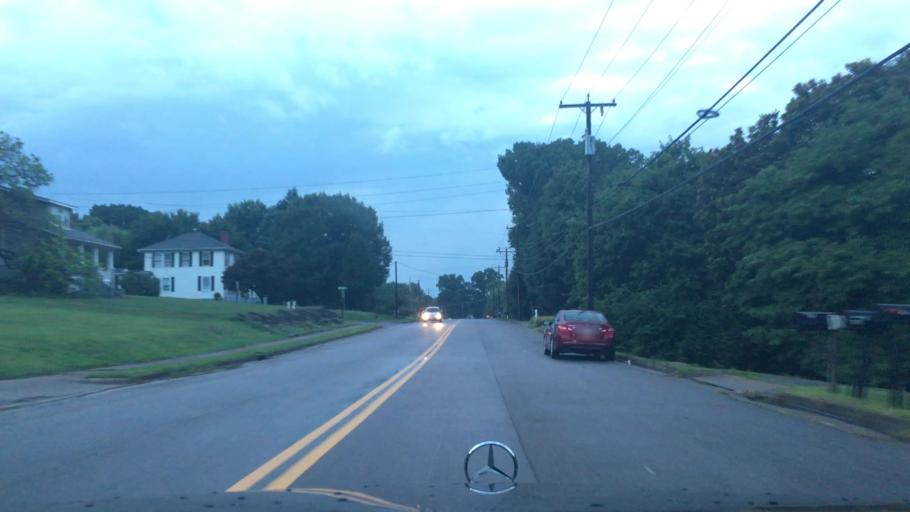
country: US
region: Virginia
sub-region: Pittsylvania County
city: Hurt
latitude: 37.0965
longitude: -79.2944
